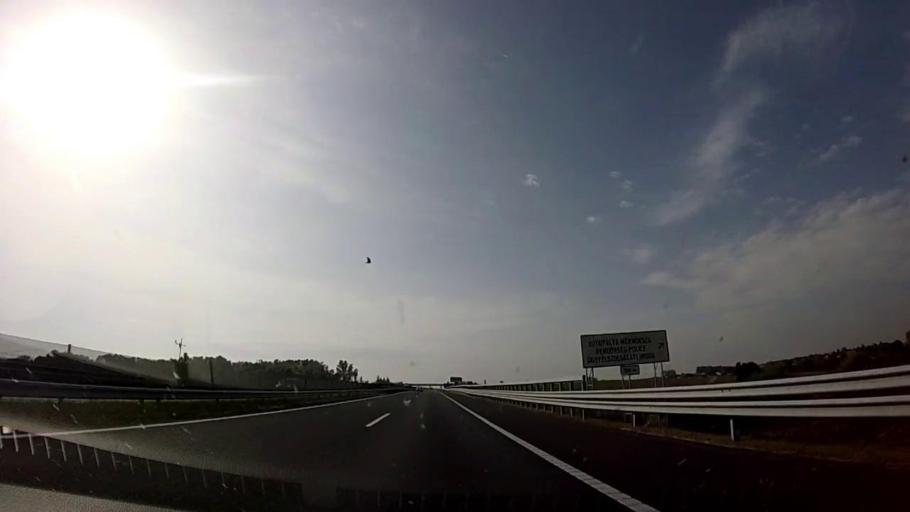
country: HU
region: Zala
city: Murakeresztur
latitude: 46.4632
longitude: 16.8913
